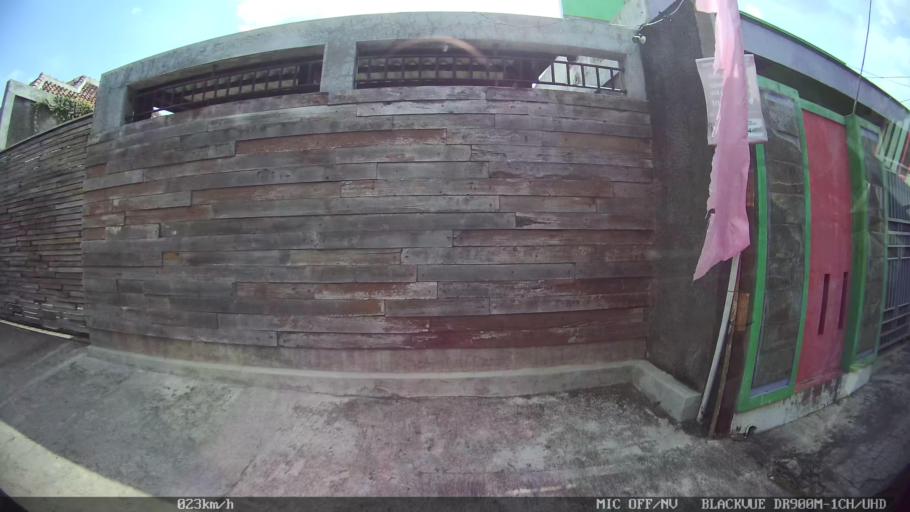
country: ID
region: Daerah Istimewa Yogyakarta
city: Kasihan
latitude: -7.8224
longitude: 110.3392
